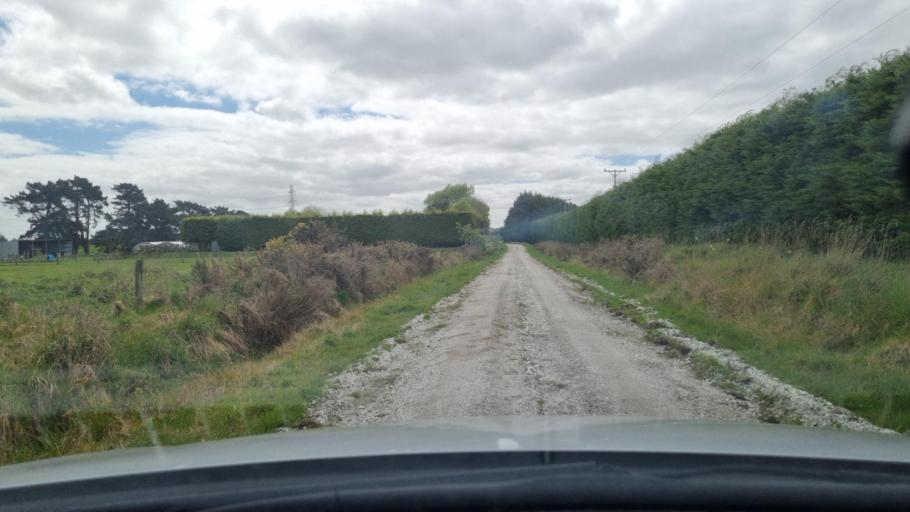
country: NZ
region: Southland
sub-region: Invercargill City
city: Invercargill
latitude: -46.3903
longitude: 168.4047
